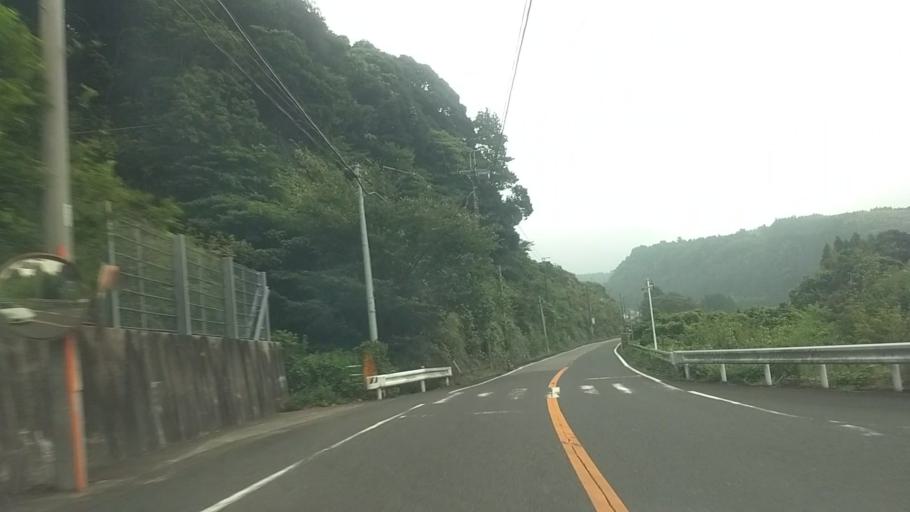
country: JP
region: Chiba
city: Katsuura
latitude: 35.2441
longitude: 140.2376
